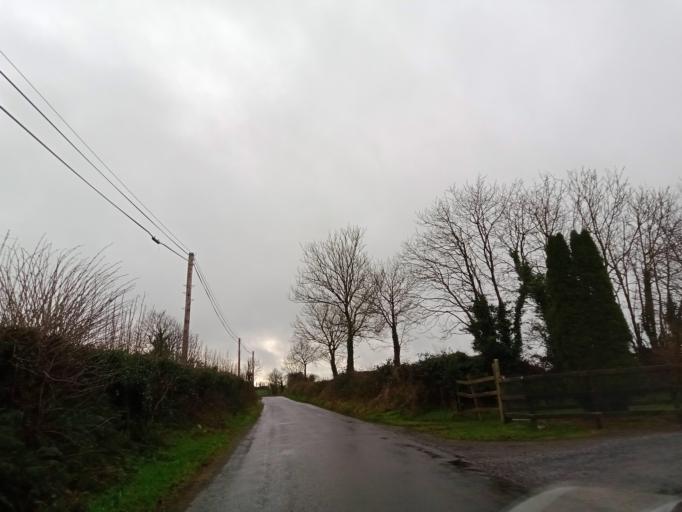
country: IE
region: Munster
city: Fethard
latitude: 52.5609
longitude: -7.6930
